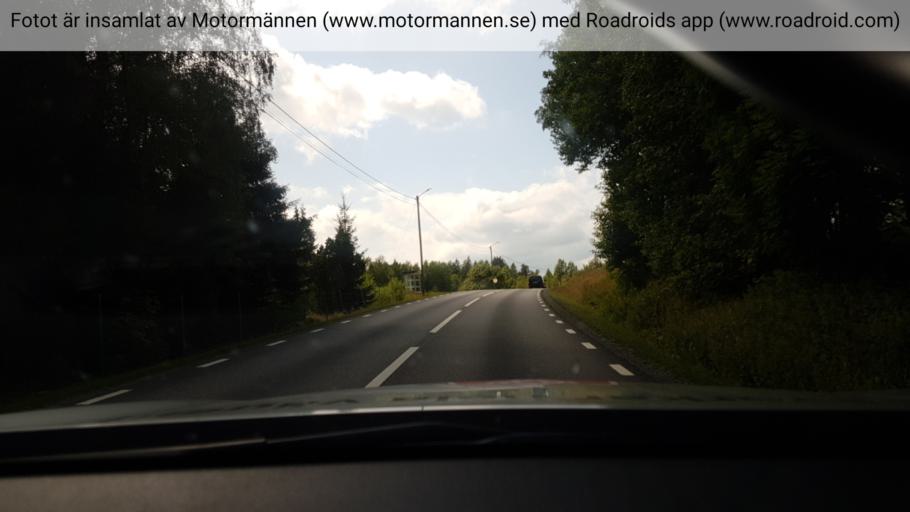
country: SE
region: Vaestra Goetaland
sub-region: Marks Kommun
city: Fritsla
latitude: 57.4816
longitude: 12.8184
